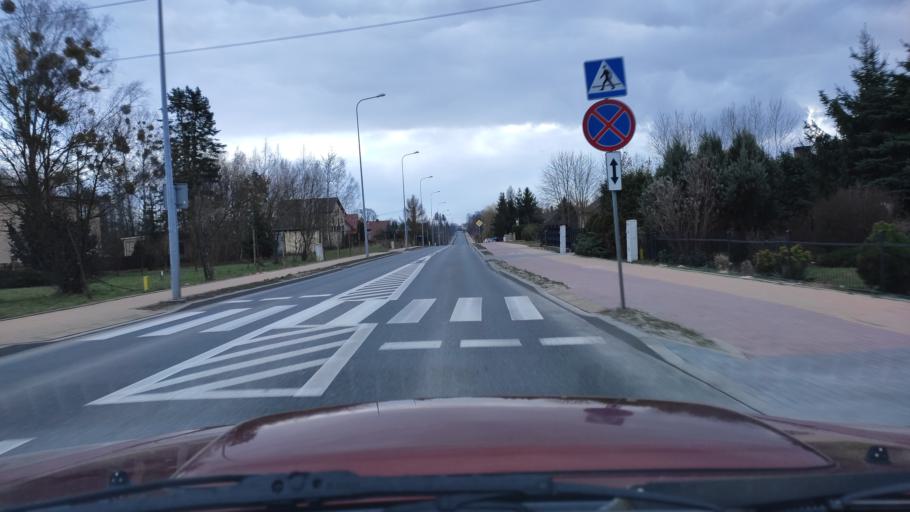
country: PL
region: Masovian Voivodeship
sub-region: Powiat zwolenski
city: Zwolen
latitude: 51.3687
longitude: 21.5857
